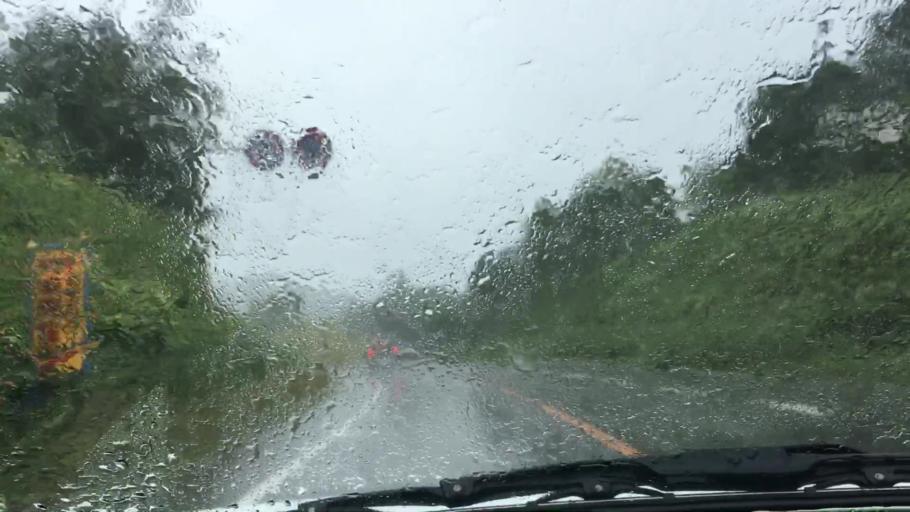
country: JP
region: Hokkaido
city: Sapporo
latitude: 42.8491
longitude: 141.0842
